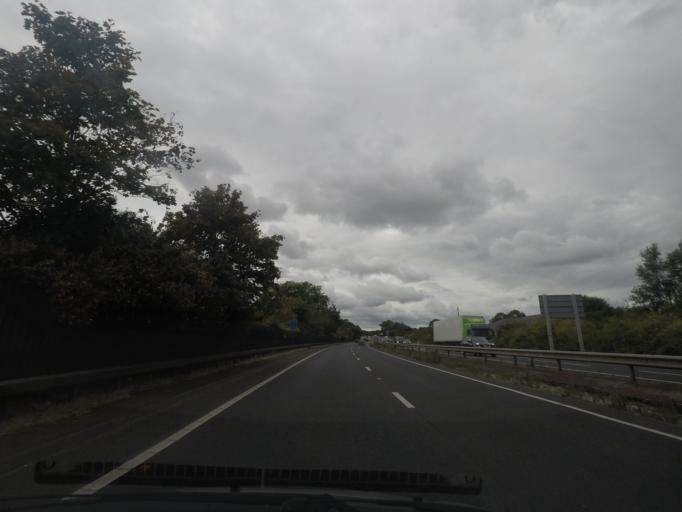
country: GB
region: England
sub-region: City of York
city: Copmanthorpe
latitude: 53.9206
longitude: -1.1402
